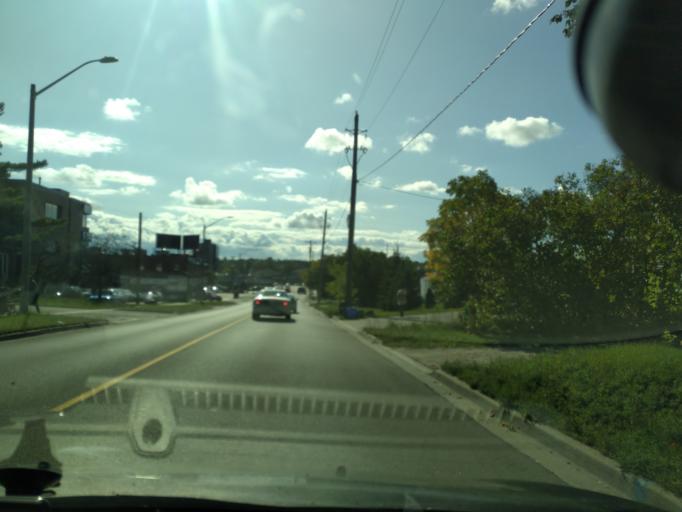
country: CA
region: Ontario
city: Barrie
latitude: 44.4034
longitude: -79.6998
